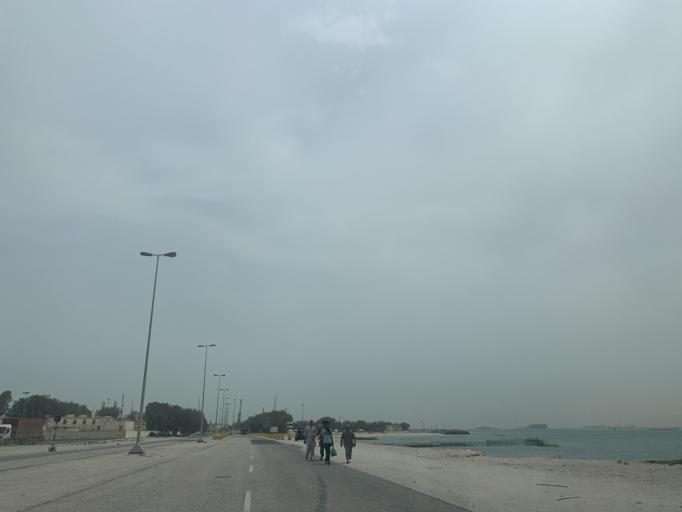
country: BH
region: Muharraq
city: Al Hadd
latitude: 26.2004
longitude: 50.6614
